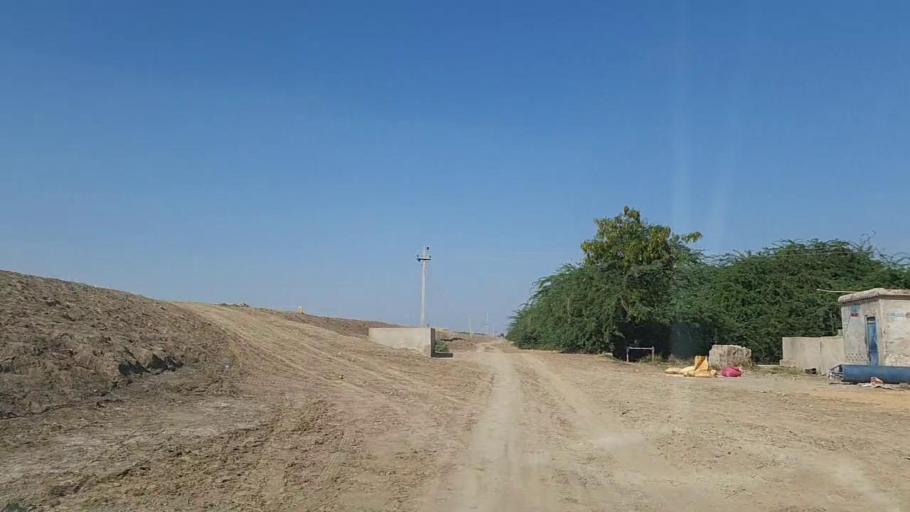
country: PK
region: Sindh
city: Chuhar Jamali
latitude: 24.5381
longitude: 68.0158
